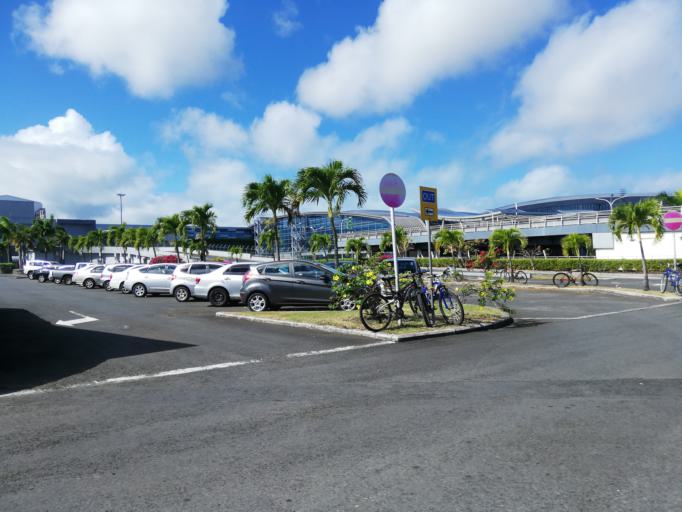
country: MU
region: Grand Port
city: Plaine Magnien
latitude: -20.4334
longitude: 57.6769
